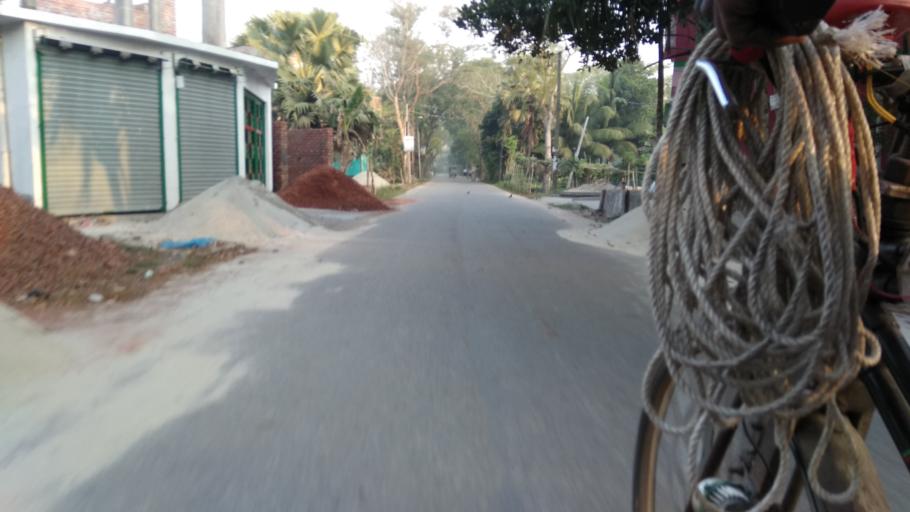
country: BD
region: Barisal
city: Mehendiganj
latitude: 22.9183
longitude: 90.4101
